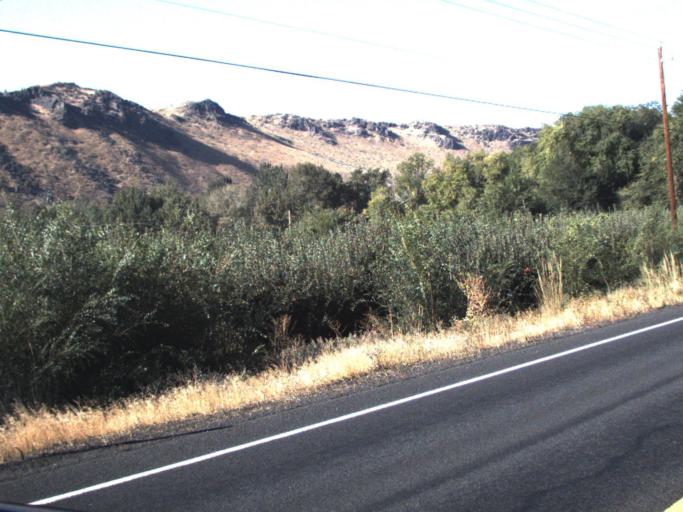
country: US
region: Washington
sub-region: Yakima County
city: Tieton
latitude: 46.7368
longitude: -120.7310
